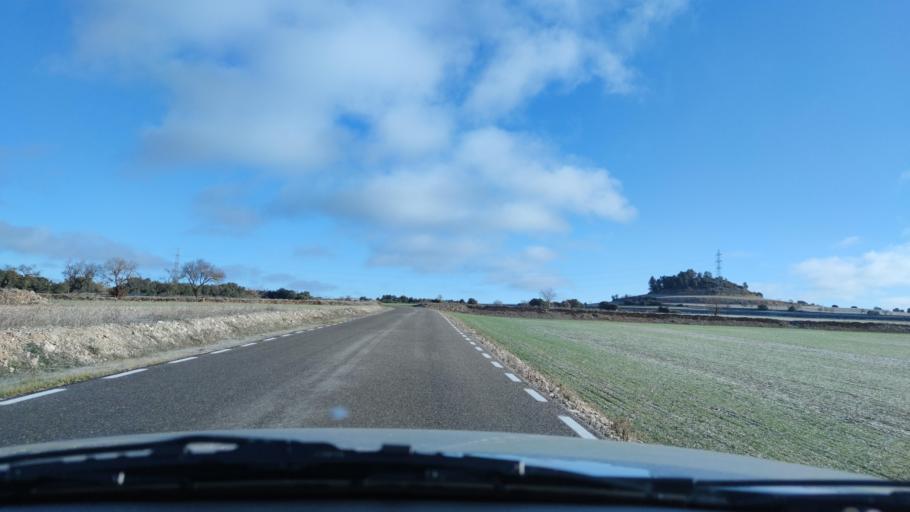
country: ES
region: Catalonia
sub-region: Provincia de Barcelona
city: Pujalt
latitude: 41.7148
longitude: 1.3570
